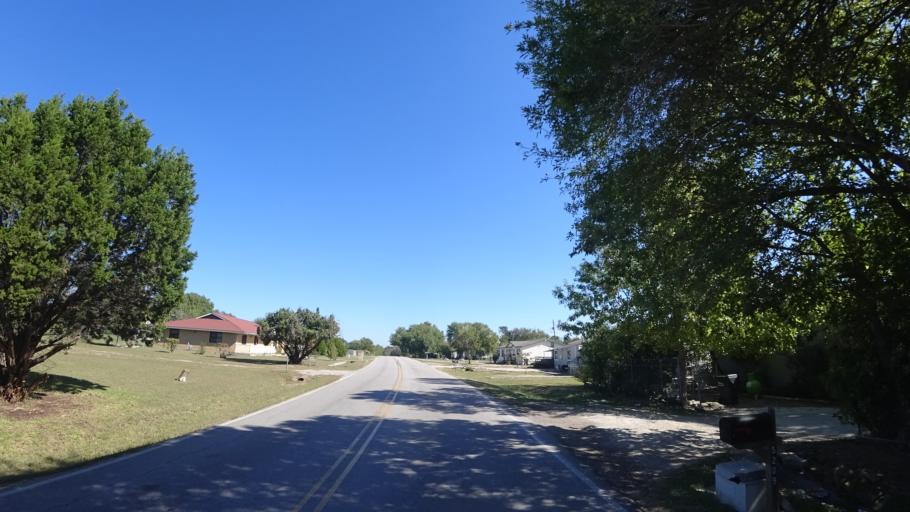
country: US
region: Texas
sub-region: Travis County
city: Hornsby Bend
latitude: 30.2703
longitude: -97.6224
